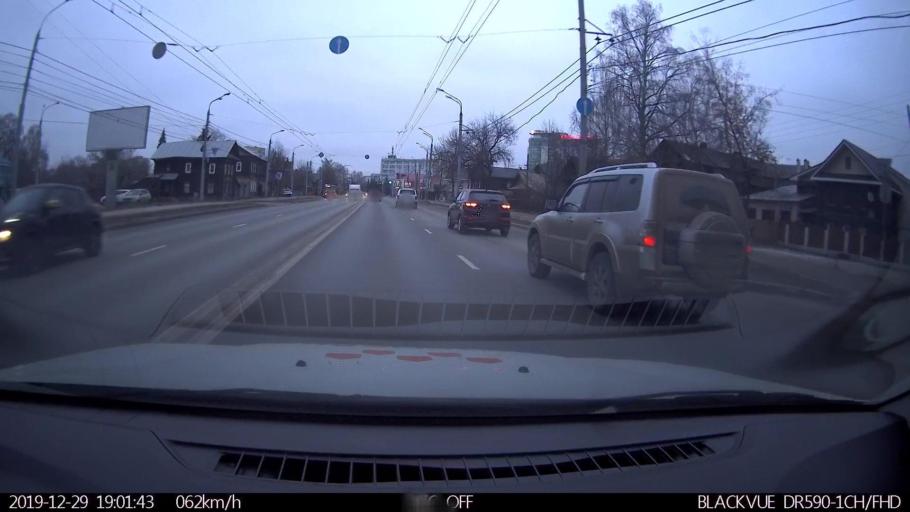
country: RU
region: Nizjnij Novgorod
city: Neklyudovo
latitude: 56.3595
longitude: 43.8634
